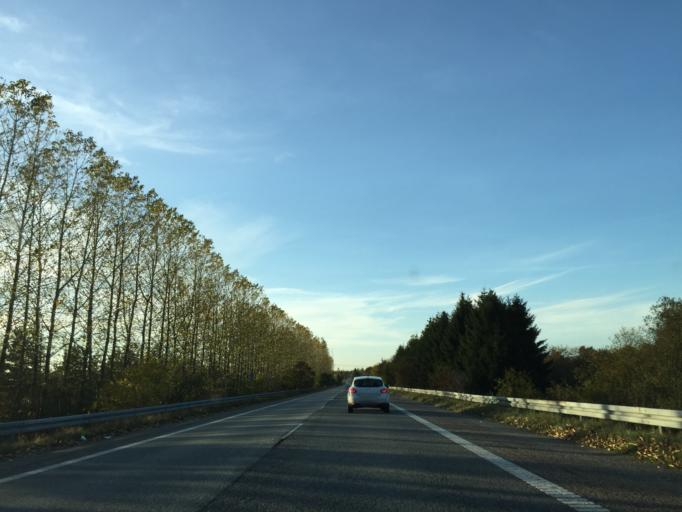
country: DK
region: South Denmark
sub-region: Aabenraa Kommune
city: Krusa
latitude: 54.8713
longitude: 9.3909
